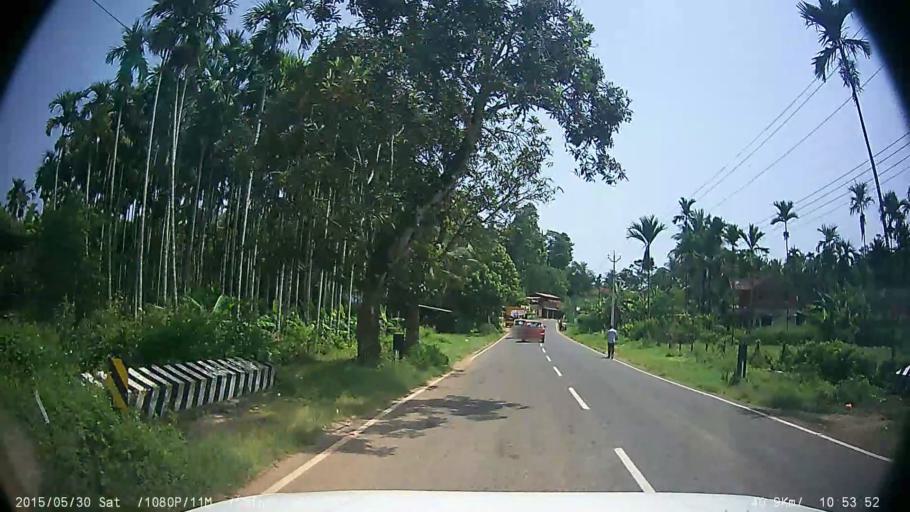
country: IN
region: Kerala
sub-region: Wayanad
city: Kalpetta
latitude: 11.6605
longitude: 76.0840
